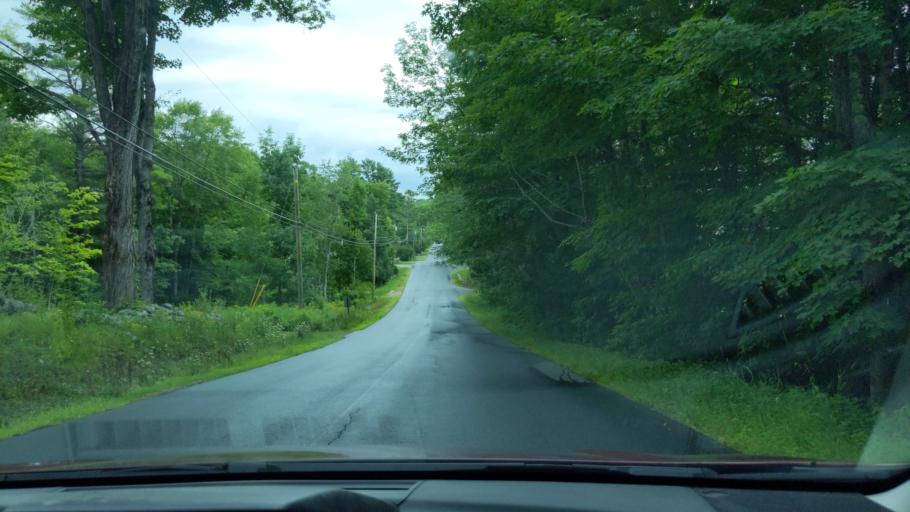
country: US
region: New Hampshire
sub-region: Merrimack County
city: New London
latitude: 43.4157
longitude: -72.0138
